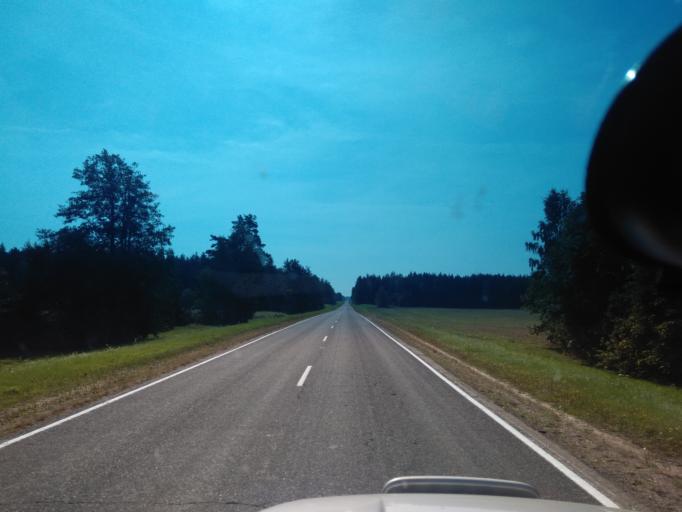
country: BY
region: Minsk
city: Uzda
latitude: 53.3345
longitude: 27.2298
